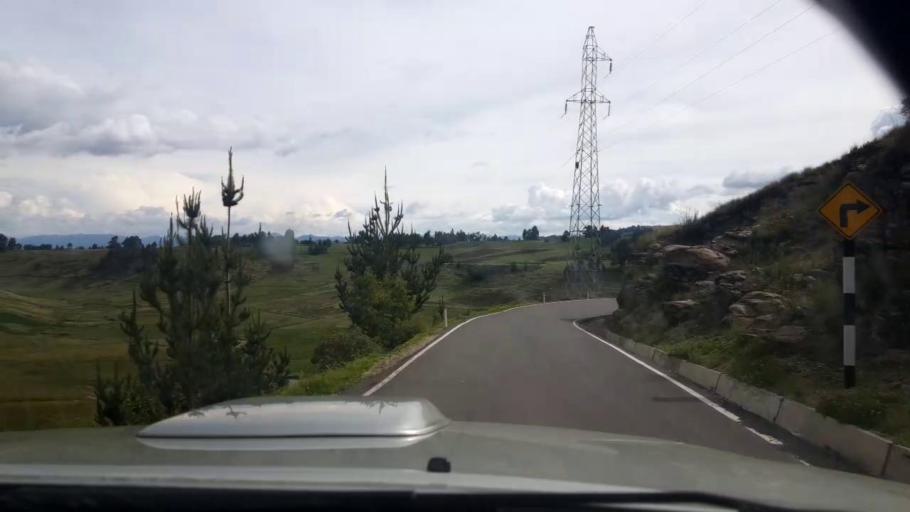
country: PE
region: Ayacucho
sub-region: Provincia de Cangallo
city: Pampa Cangallo
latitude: -13.4504
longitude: -74.1988
